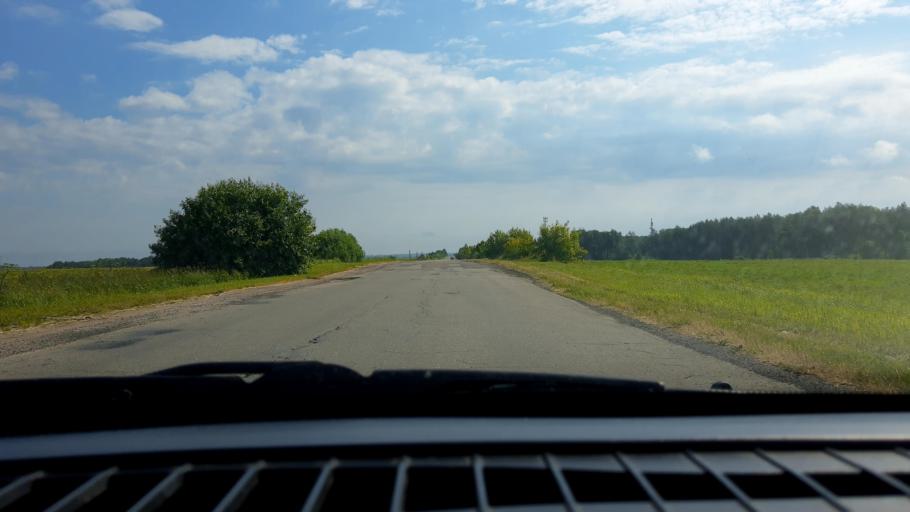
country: RU
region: Nizjnij Novgorod
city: Kstovo
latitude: 56.1124
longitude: 44.2977
